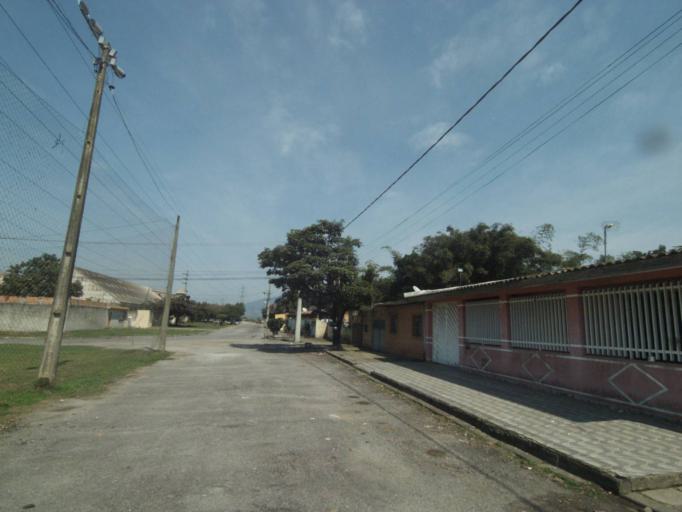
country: BR
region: Parana
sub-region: Paranagua
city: Paranagua
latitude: -25.5349
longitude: -48.5360
